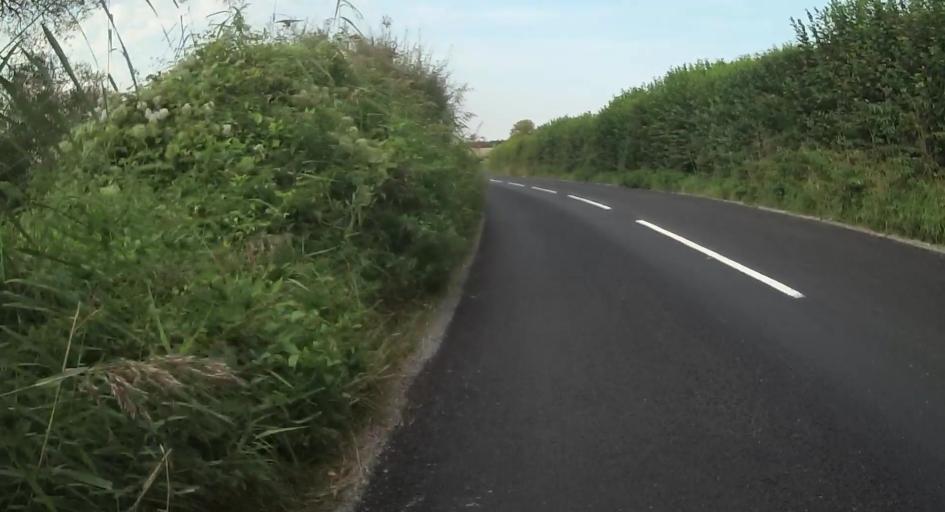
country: GB
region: England
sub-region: Hampshire
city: Swanmore
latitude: 51.0613
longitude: -1.1721
